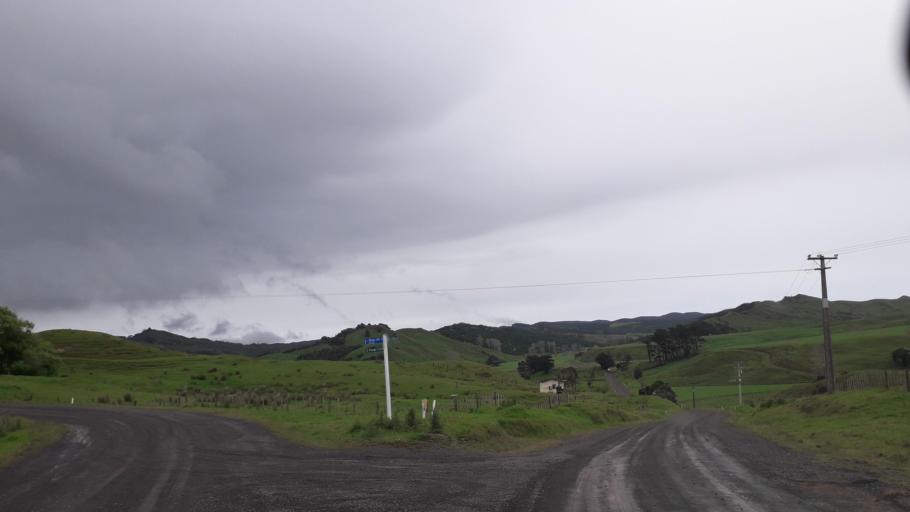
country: NZ
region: Northland
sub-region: Far North District
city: Kaitaia
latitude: -35.4140
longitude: 173.3664
